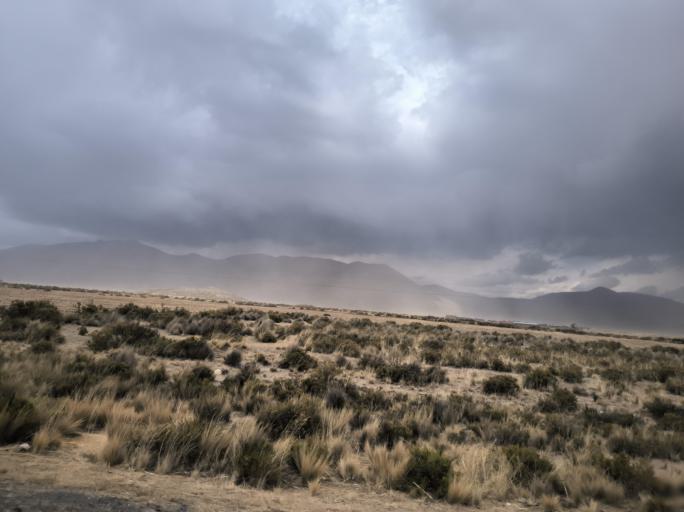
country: BO
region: Oruro
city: Challapata
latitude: -18.7711
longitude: -66.8559
